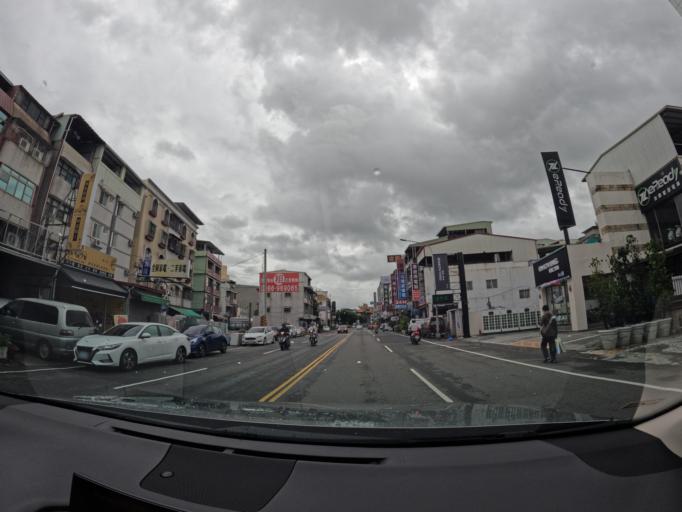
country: TW
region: Taiwan
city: Fengshan
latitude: 22.6276
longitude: 120.3496
